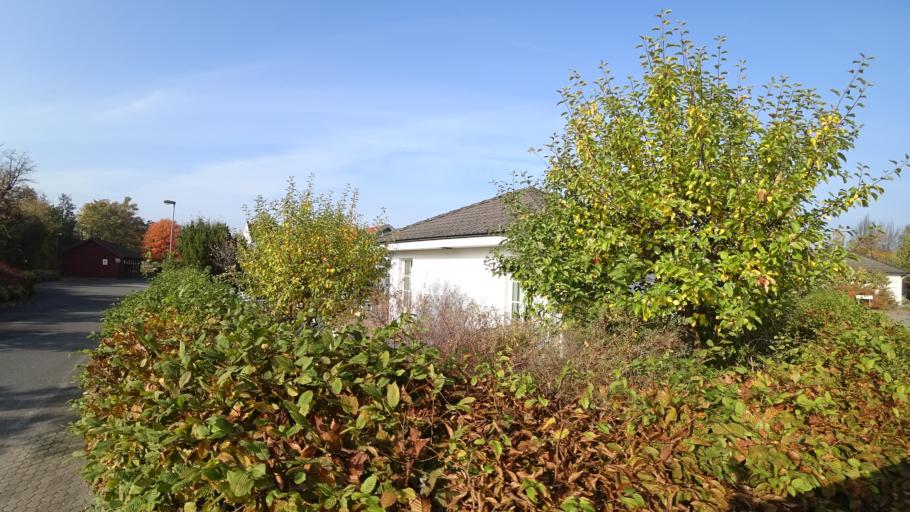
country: SE
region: Skane
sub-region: Staffanstorps Kommun
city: Staffanstorp
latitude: 55.6525
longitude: 13.2182
